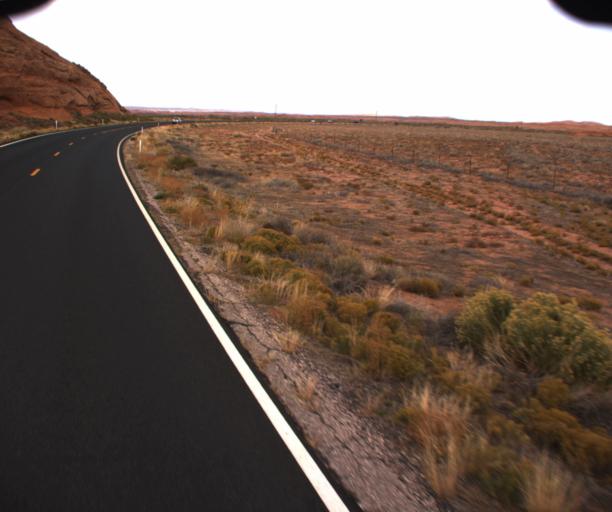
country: US
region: Arizona
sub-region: Apache County
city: Many Farms
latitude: 36.7698
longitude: -109.6592
